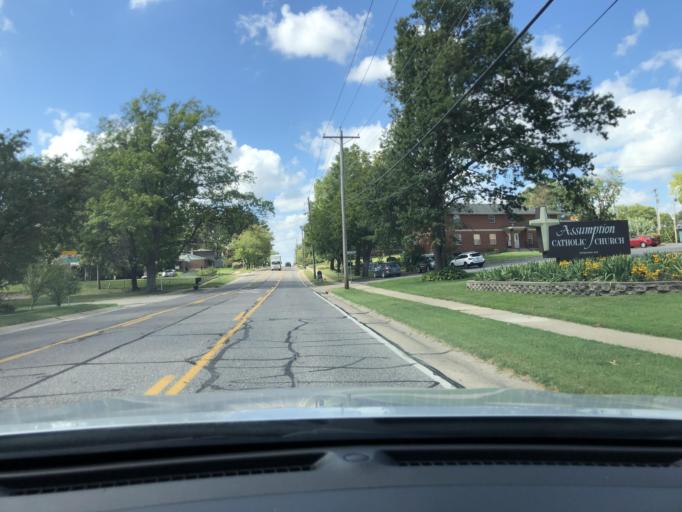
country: US
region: Missouri
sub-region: Saint Louis County
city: Concord
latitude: 38.5003
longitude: -90.3604
